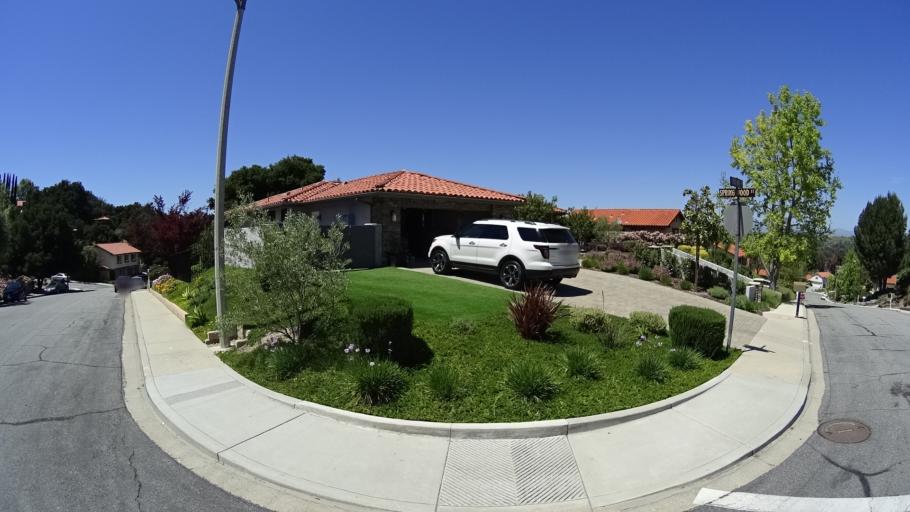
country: US
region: California
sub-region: Ventura County
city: Casa Conejo
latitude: 34.1750
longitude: -118.8972
